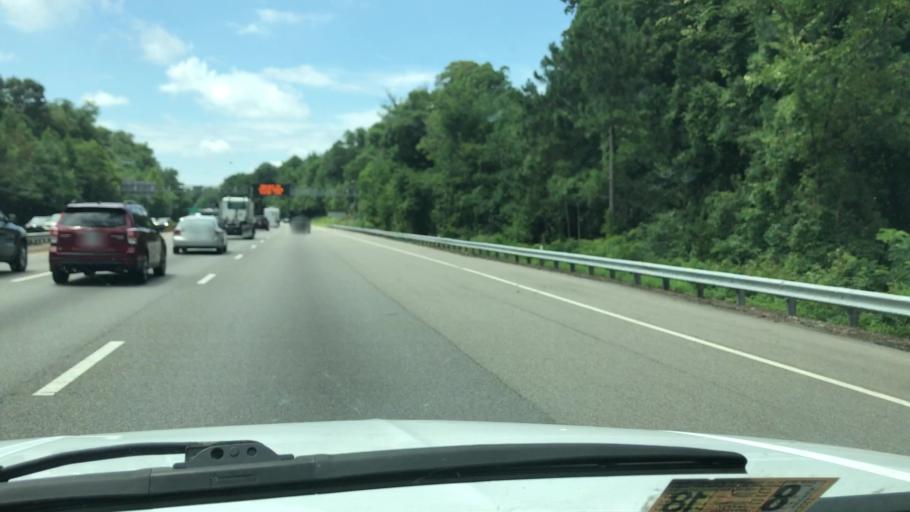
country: US
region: Virginia
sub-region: Henrico County
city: Lakeside
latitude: 37.6094
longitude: -77.4507
